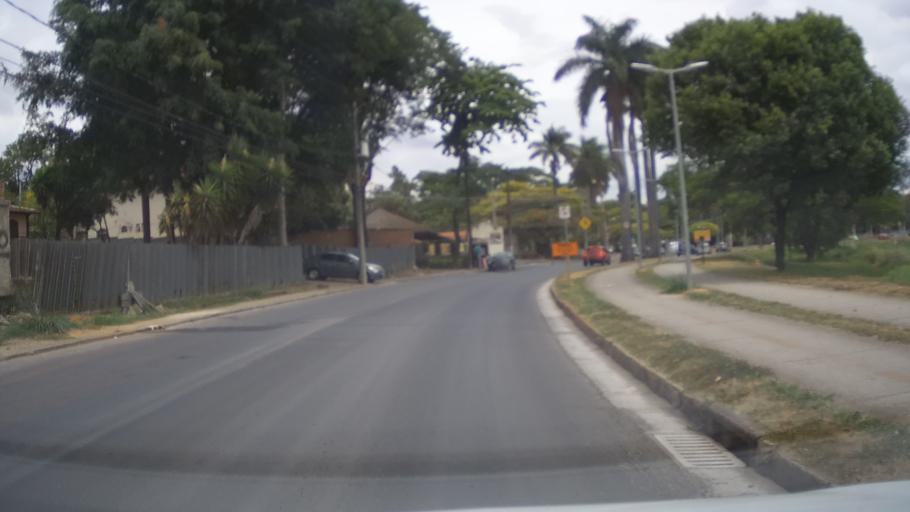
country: BR
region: Minas Gerais
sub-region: Contagem
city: Contagem
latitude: -19.8539
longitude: -44.0035
